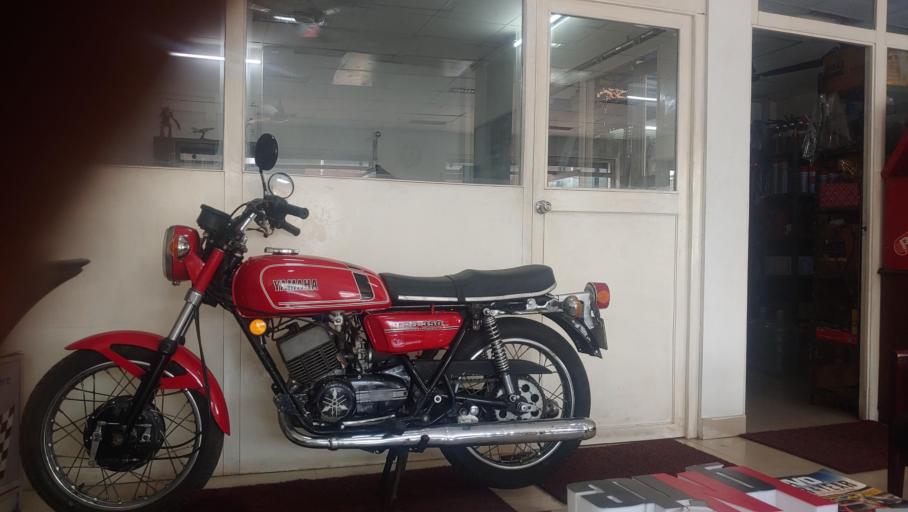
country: IN
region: Tamil Nadu
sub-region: Kancheepuram
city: Injambakkam
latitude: 12.9015
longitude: 80.2484
